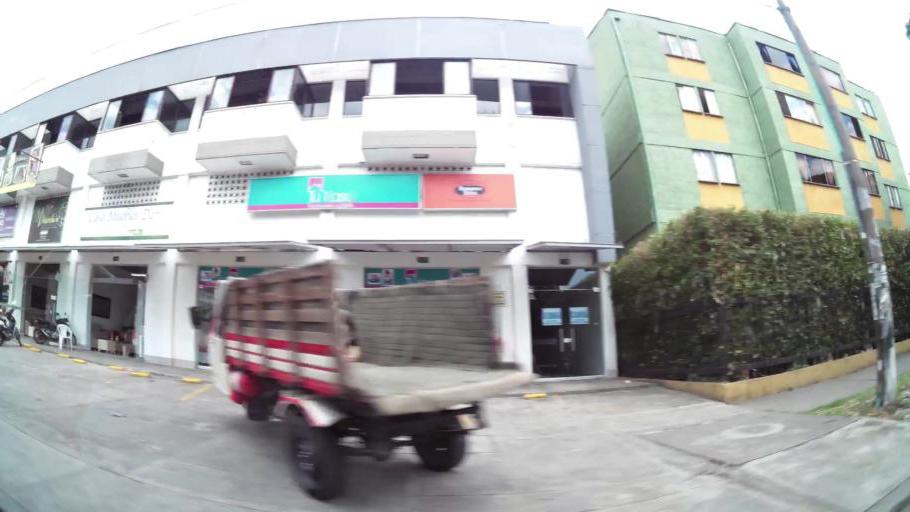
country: CO
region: Valle del Cauca
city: Cali
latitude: 3.4670
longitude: -76.5087
